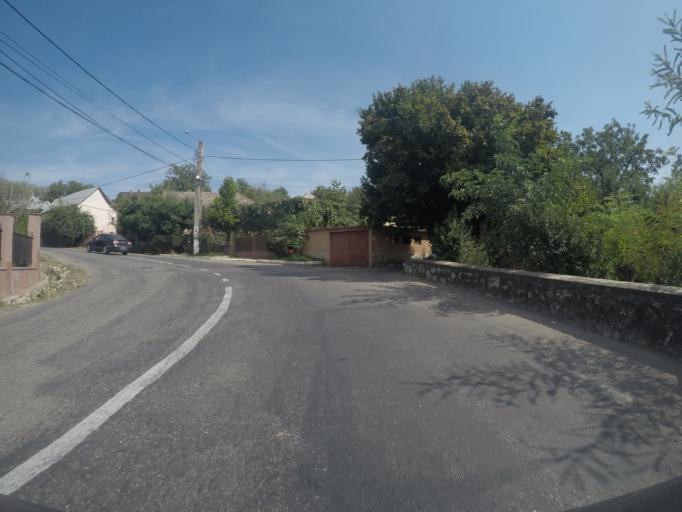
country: RO
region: Cluj
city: Turda
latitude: 46.5751
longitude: 23.7901
